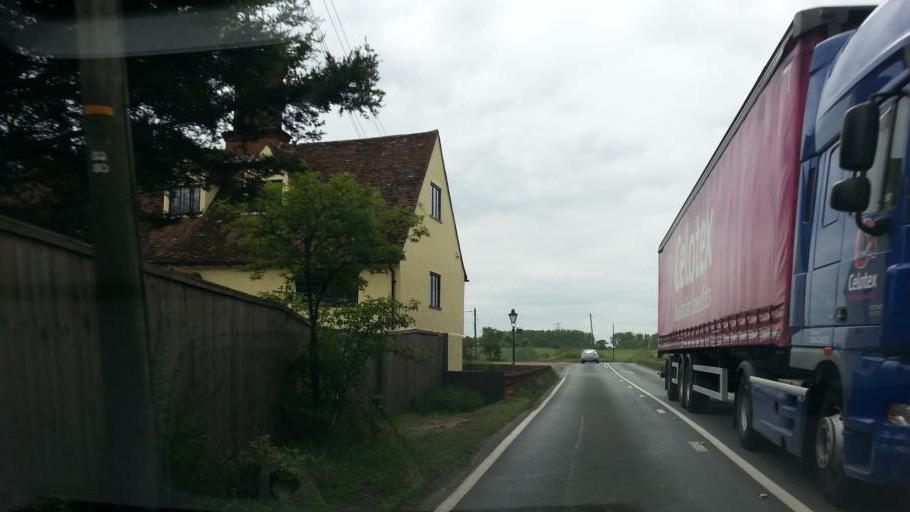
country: GB
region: England
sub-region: Suffolk
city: Bramford
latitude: 52.0523
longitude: 1.0715
